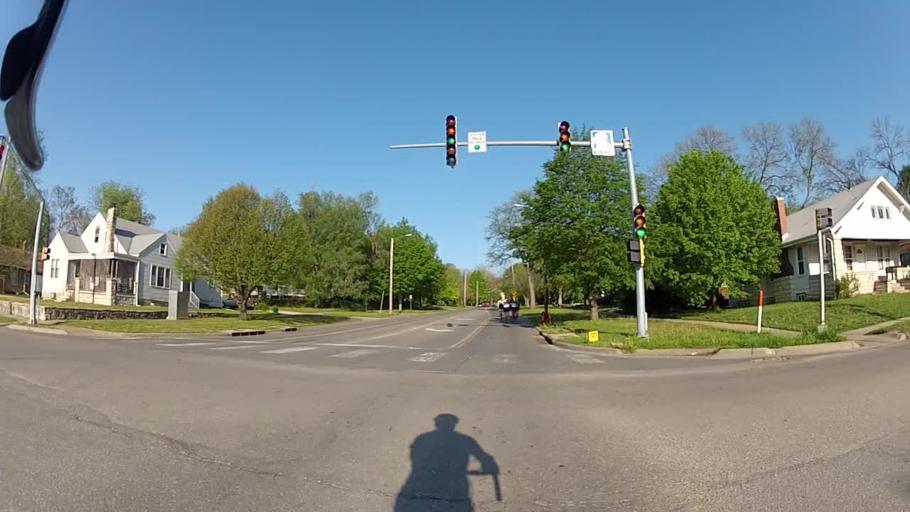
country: US
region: Kansas
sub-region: Riley County
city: Manhattan
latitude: 39.1796
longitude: -96.5833
